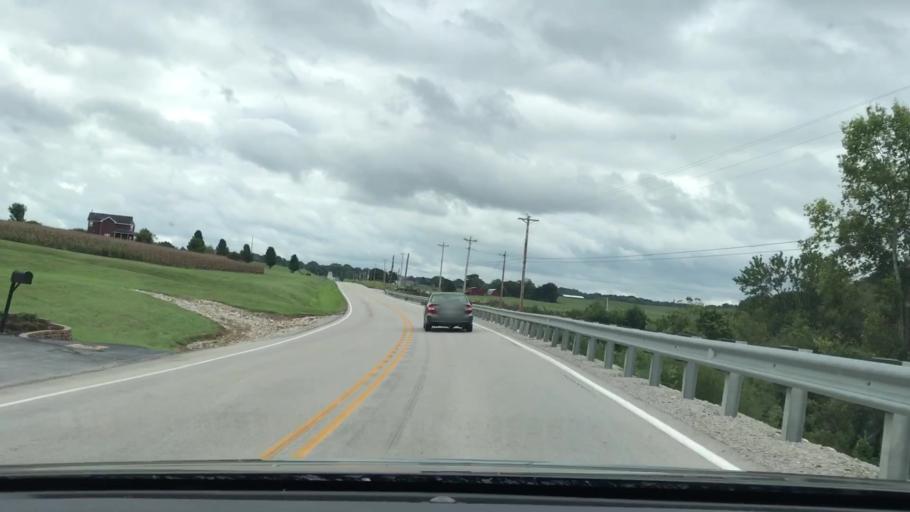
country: US
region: Kentucky
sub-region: Barren County
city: Glasgow
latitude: 36.9234
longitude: -85.8031
